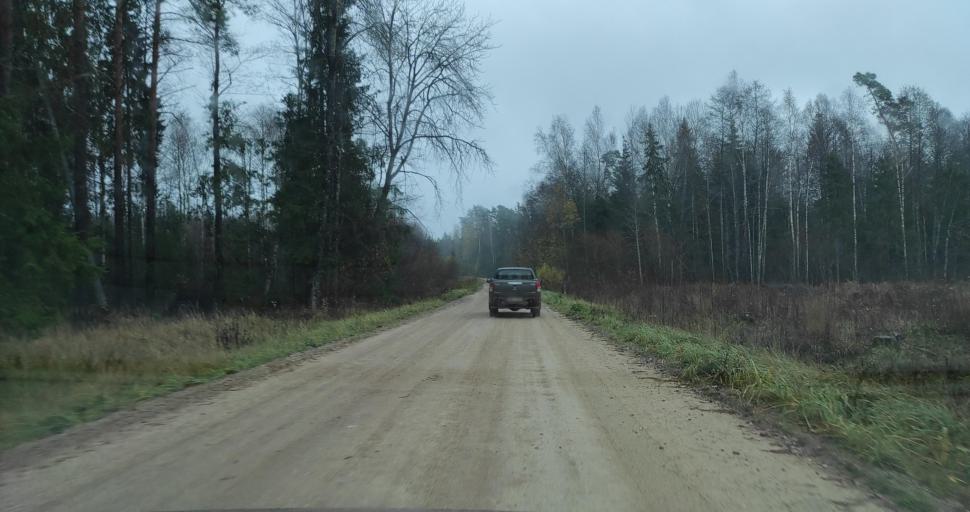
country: LV
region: Skrunda
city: Skrunda
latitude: 56.6929
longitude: 22.0867
